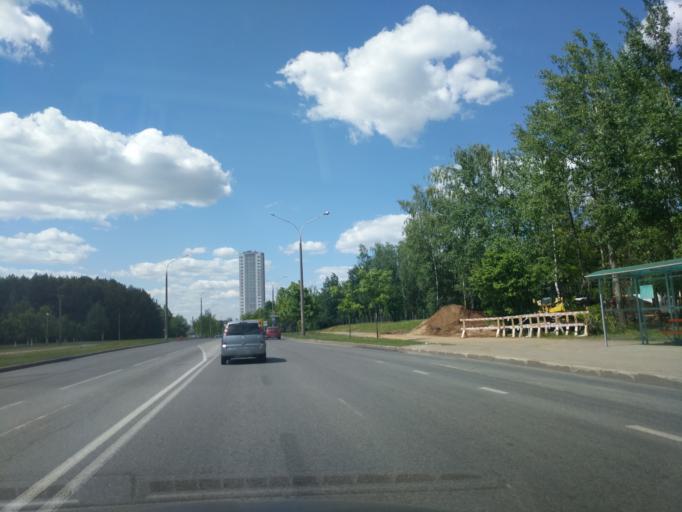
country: BY
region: Minsk
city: Borovlyany
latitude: 53.9260
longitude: 27.6616
